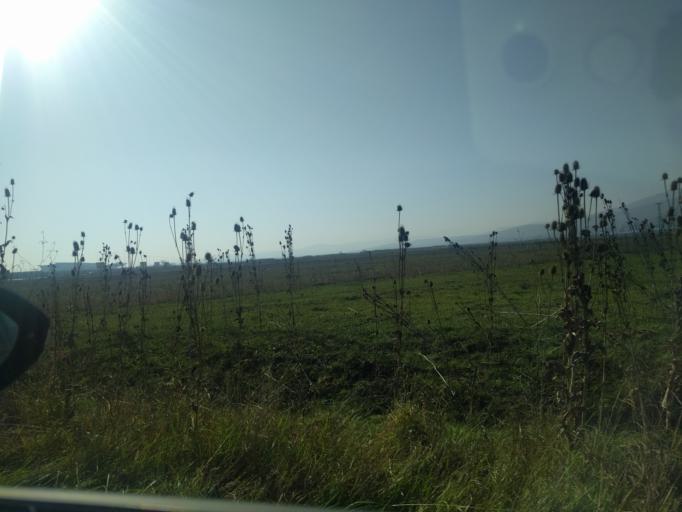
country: XK
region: Pristina
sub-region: Komuna e Gracanices
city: Glanica
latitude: 42.5839
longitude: 21.0256
